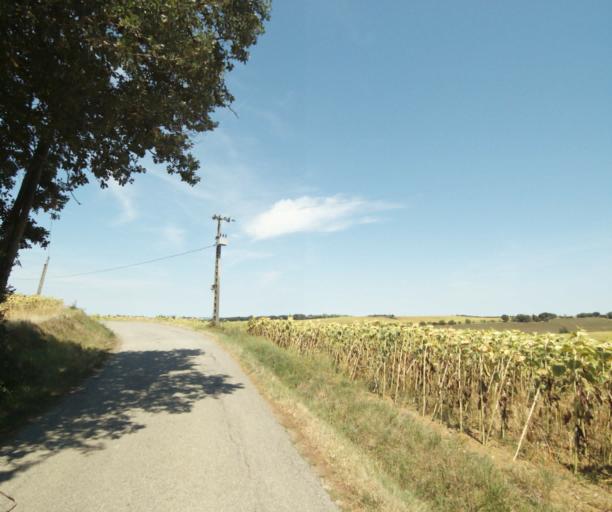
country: FR
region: Midi-Pyrenees
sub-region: Departement de l'Ariege
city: Lezat-sur-Leze
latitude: 43.2820
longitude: 1.3045
